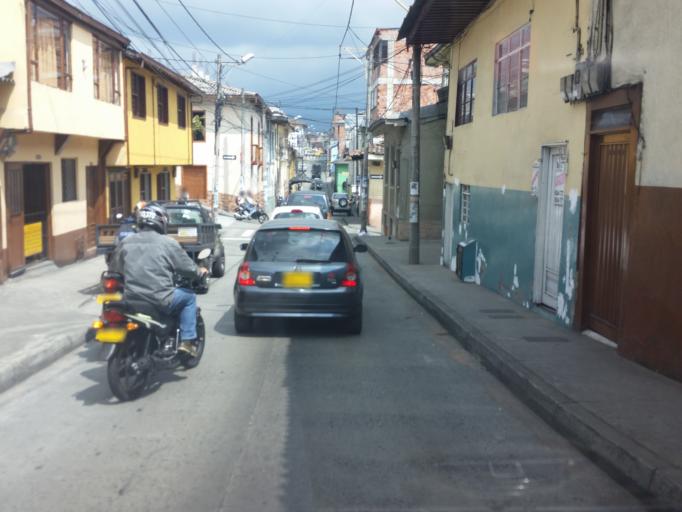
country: CO
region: Caldas
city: Manizales
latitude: 5.0659
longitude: -75.5166
